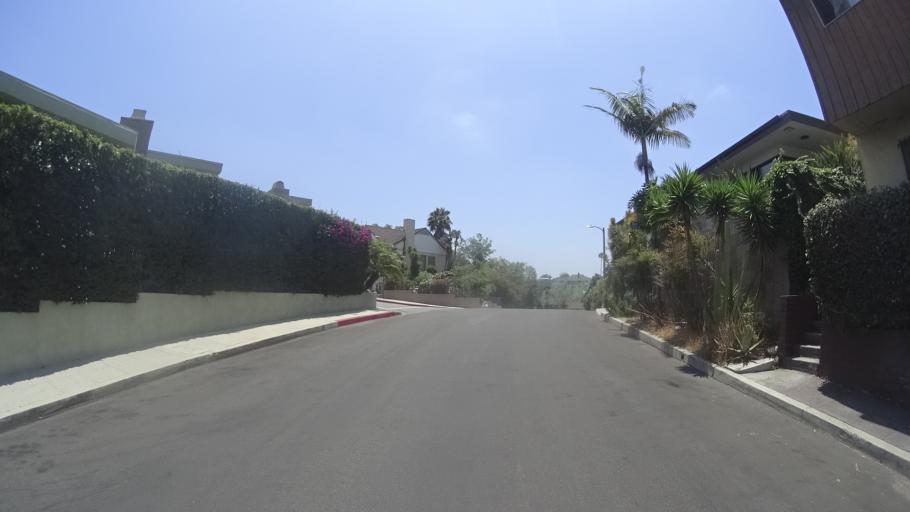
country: US
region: California
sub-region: Los Angeles County
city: View Park-Windsor Hills
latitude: 34.0083
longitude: -118.3482
